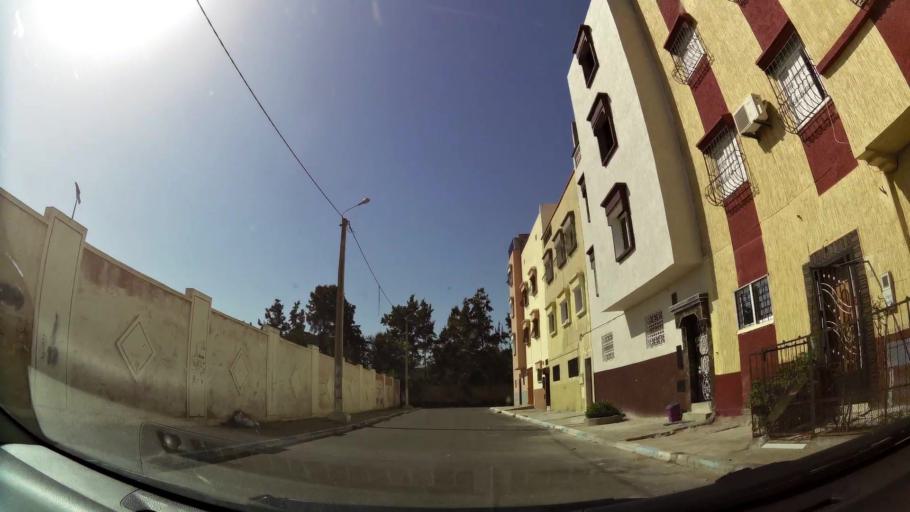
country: MA
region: Souss-Massa-Draa
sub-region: Inezgane-Ait Mellou
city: Inezgane
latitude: 30.3567
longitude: -9.5539
